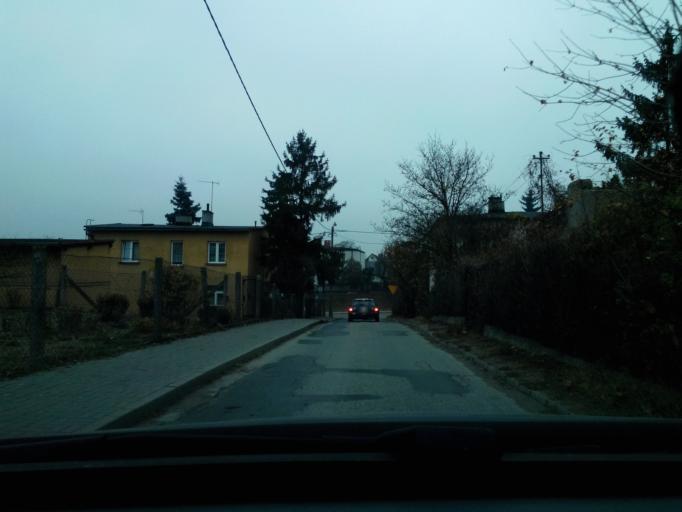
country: PL
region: Kujawsko-Pomorskie
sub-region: Powiat brodnicki
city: Brodnica
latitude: 53.2676
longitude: 19.4076
